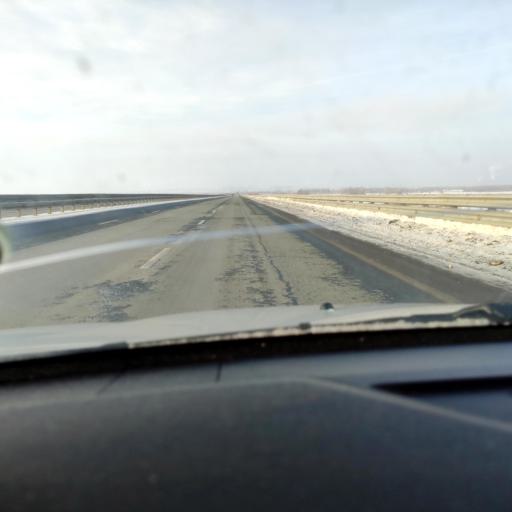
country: RU
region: Samara
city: Smyshlyayevka
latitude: 53.1524
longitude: 50.3530
